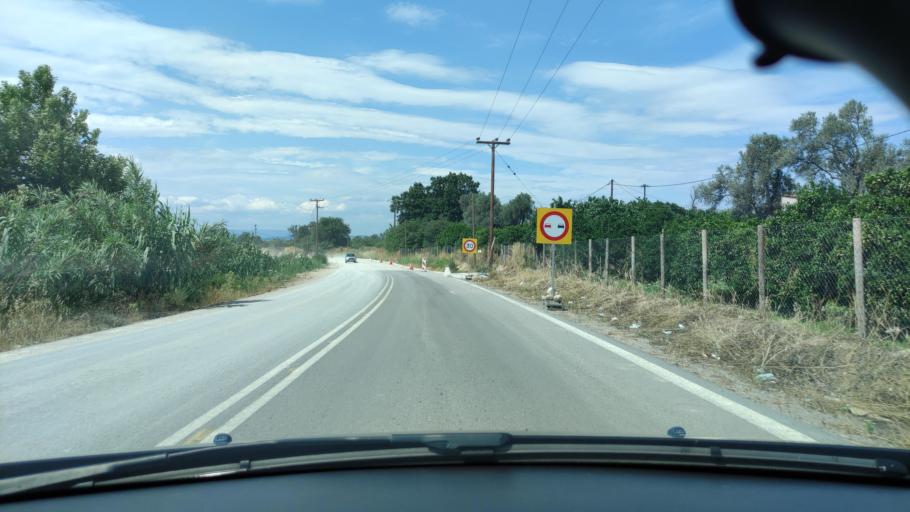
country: GR
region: Central Greece
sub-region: Nomos Evvoias
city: Vasilikon
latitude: 38.4395
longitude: 23.6676
